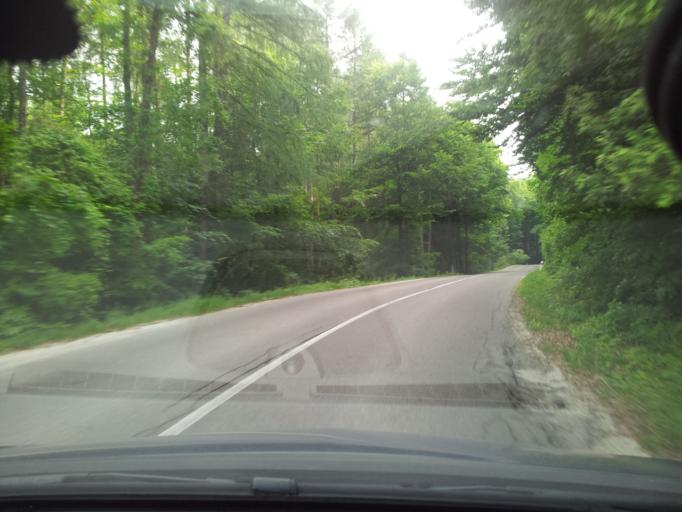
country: SK
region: Nitriansky
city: Partizanske
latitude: 48.5306
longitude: 18.4405
